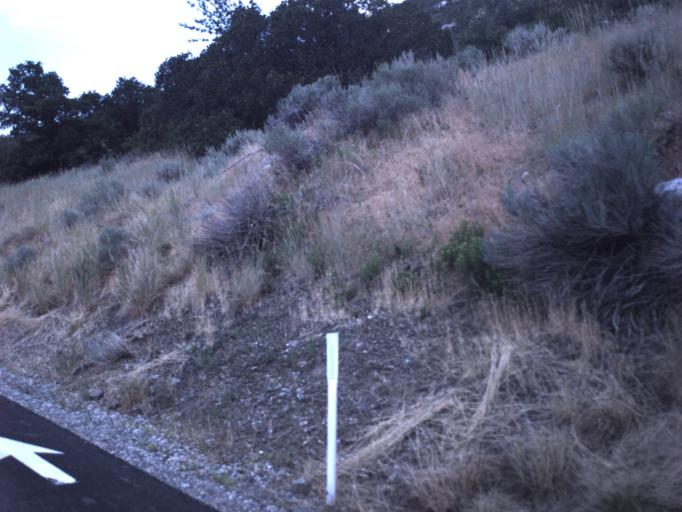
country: US
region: Utah
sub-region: Salt Lake County
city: Granite
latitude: 40.5777
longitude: -111.7894
